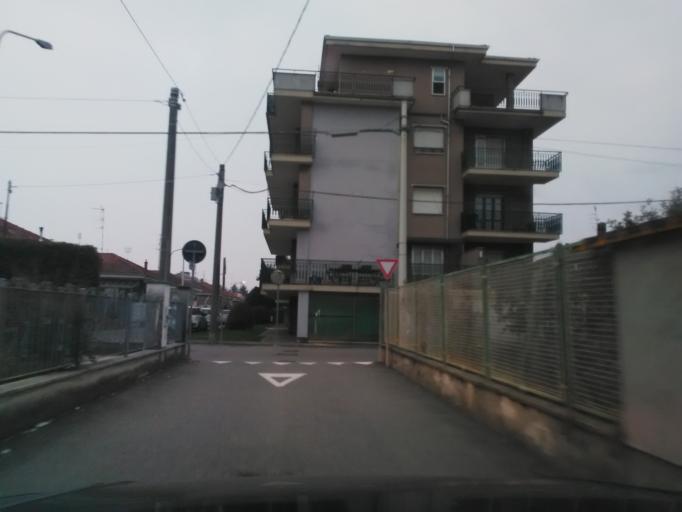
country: IT
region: Piedmont
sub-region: Provincia di Vercelli
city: Santhia
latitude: 45.3700
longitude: 8.1657
